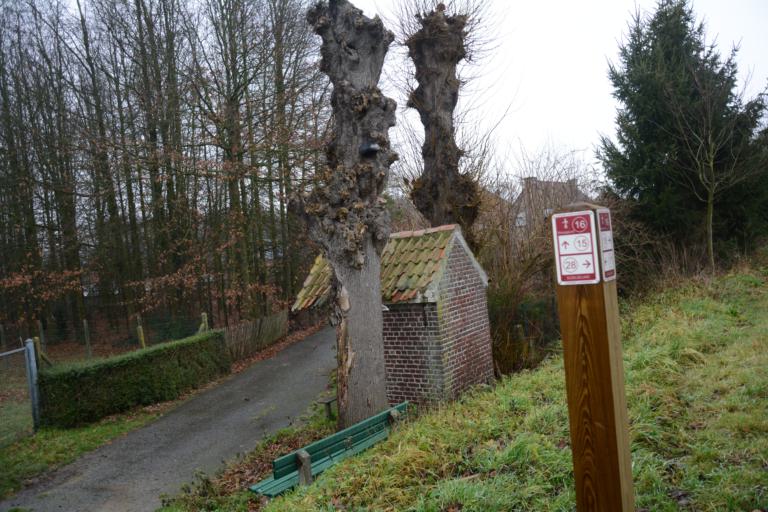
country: BE
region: Flanders
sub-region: Provincie Oost-Vlaanderen
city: Lebbeke
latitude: 50.9618
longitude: 4.1293
